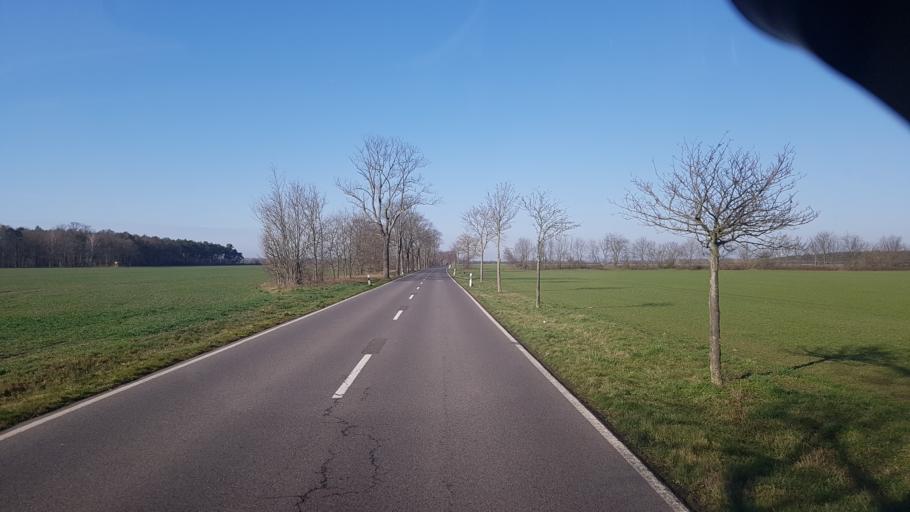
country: DE
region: Brandenburg
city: Luckau
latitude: 51.8497
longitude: 13.7954
